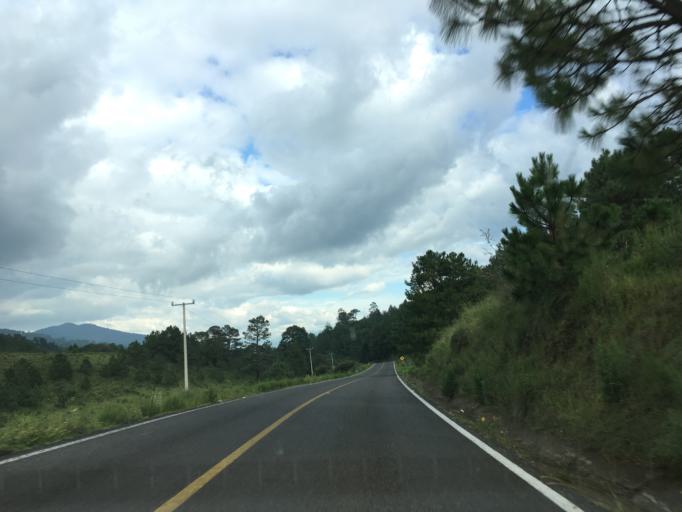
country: MX
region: Michoacan
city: Pichataro
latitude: 19.6022
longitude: -101.8396
